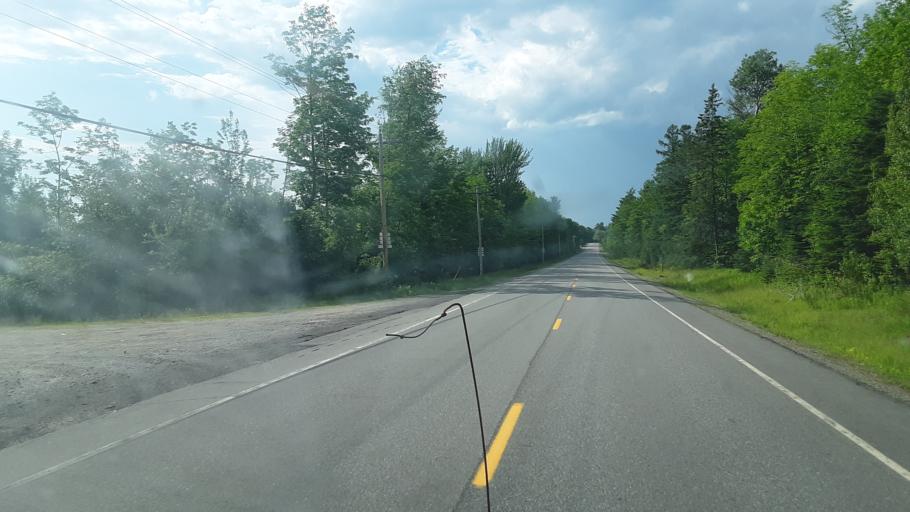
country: US
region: Maine
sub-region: Washington County
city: Machias
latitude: 45.0160
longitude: -67.5567
